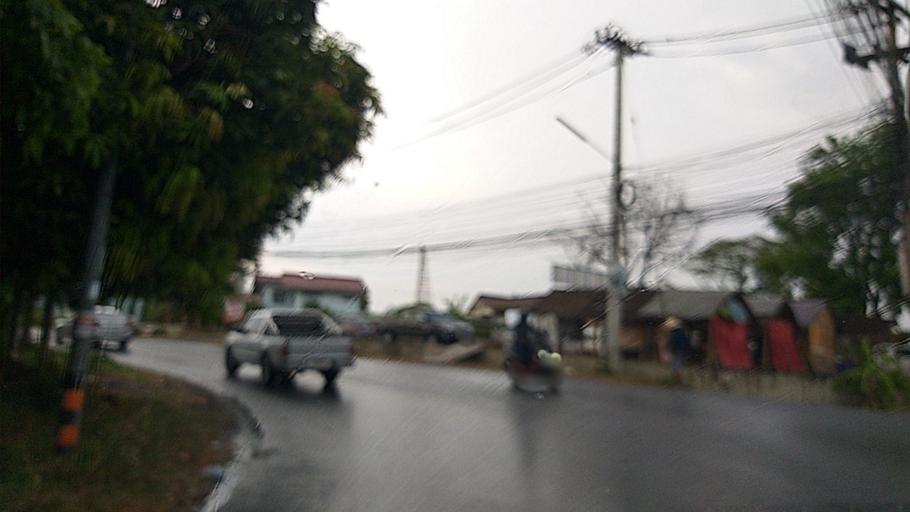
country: TH
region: Phra Nakhon Si Ayutthaya
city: Phra Nakhon Si Ayutthaya
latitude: 14.3443
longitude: 100.5421
